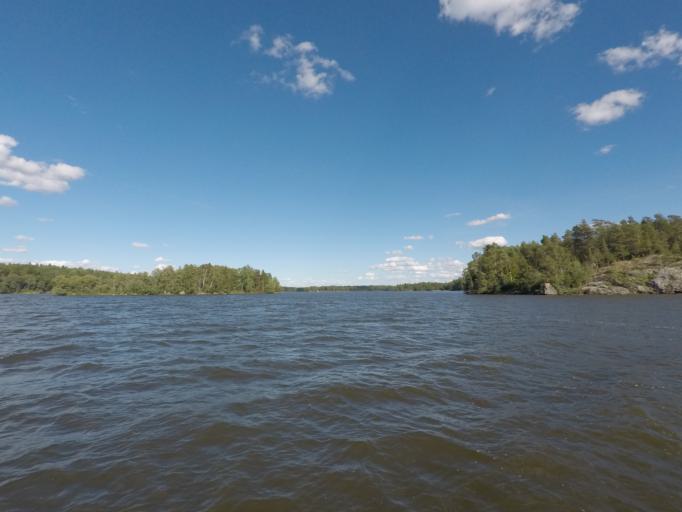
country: SE
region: Soedermanland
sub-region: Eskilstuna Kommun
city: Kvicksund
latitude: 59.4787
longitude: 16.3971
